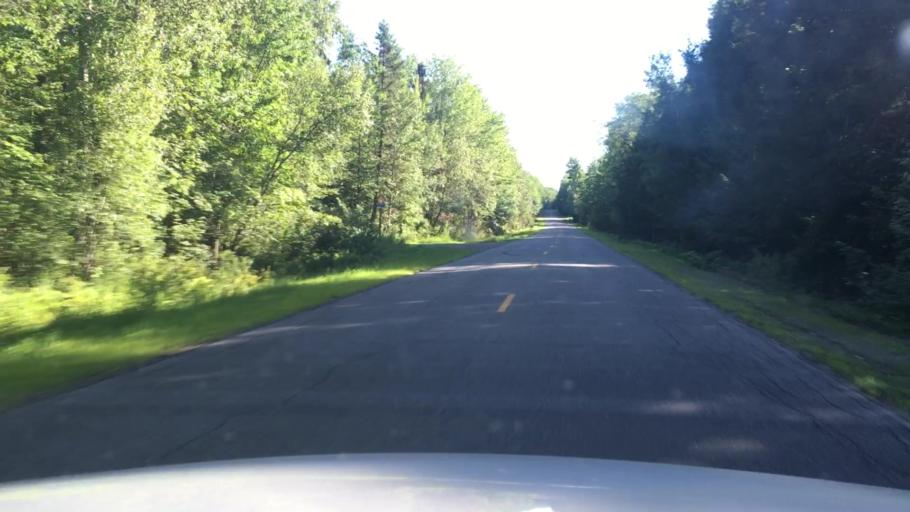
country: US
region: Maine
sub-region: Penobscot County
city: Enfield
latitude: 45.2178
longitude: -68.5835
